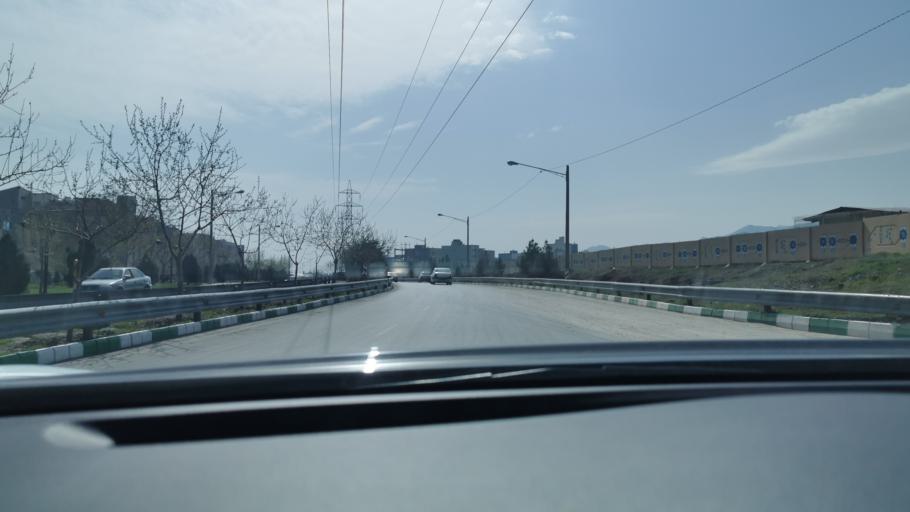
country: IR
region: Razavi Khorasan
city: Mashhad
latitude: 36.2849
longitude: 59.5406
